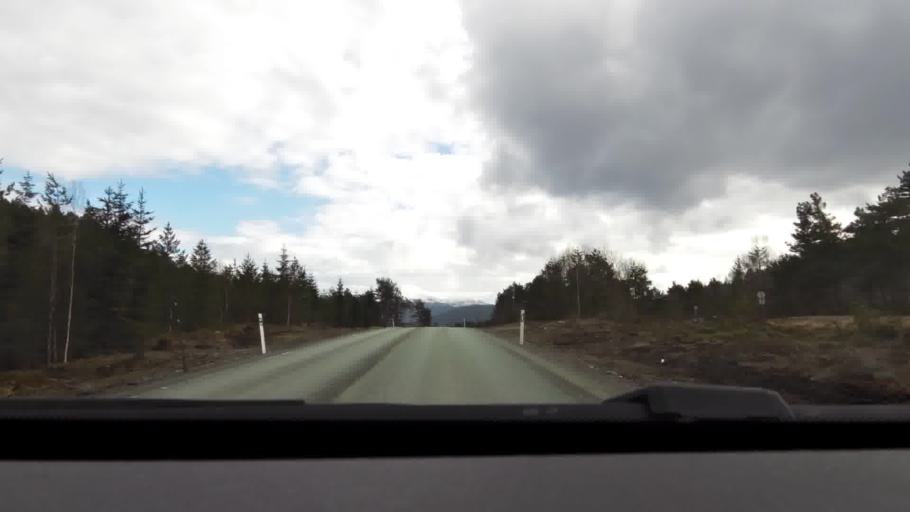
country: NO
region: More og Romsdal
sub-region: Kristiansund
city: Rensvik
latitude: 63.0436
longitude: 7.7859
